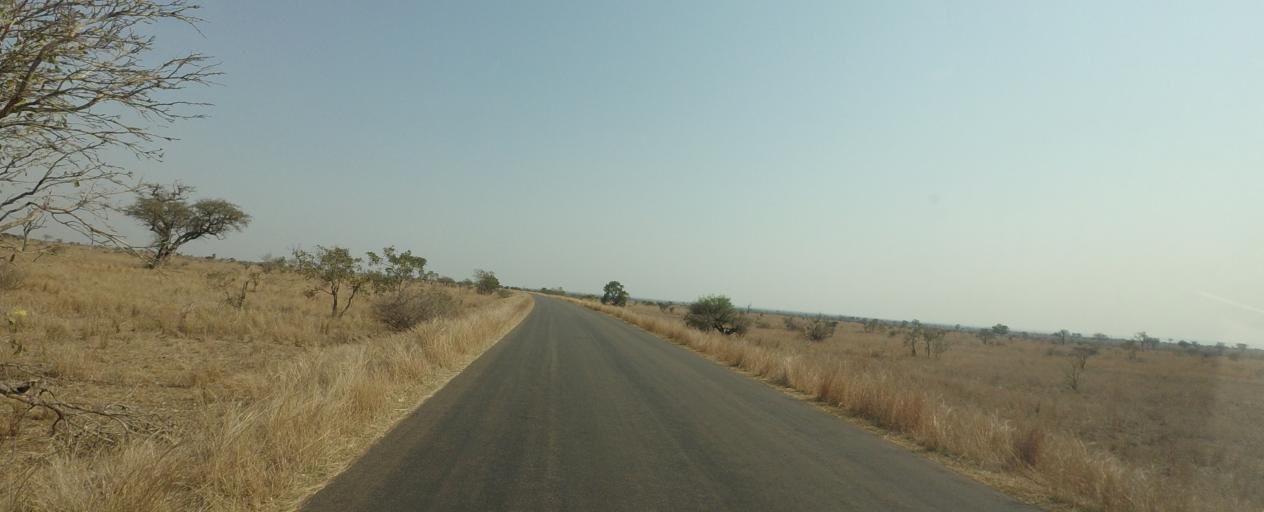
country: ZA
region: Limpopo
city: Thulamahashi
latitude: -24.3300
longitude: 31.7558
